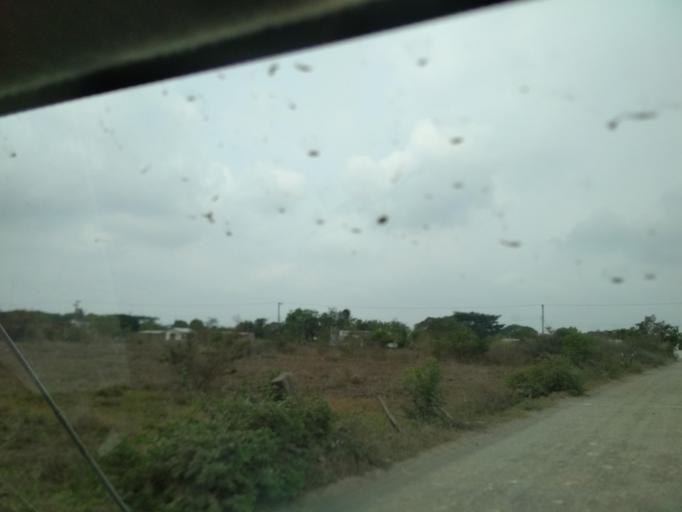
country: MX
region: Veracruz
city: Paso del Toro
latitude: 19.0124
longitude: -96.1095
